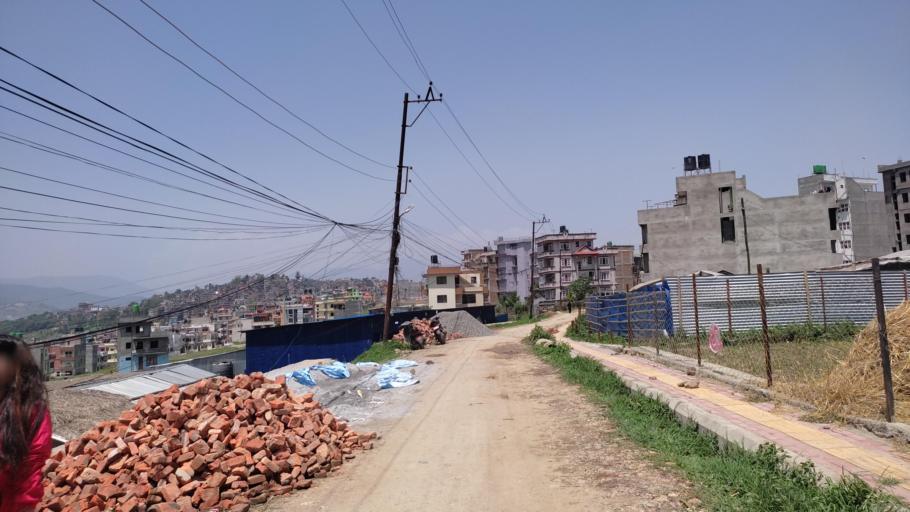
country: NP
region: Central Region
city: Kirtipur
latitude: 27.6708
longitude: 85.2694
